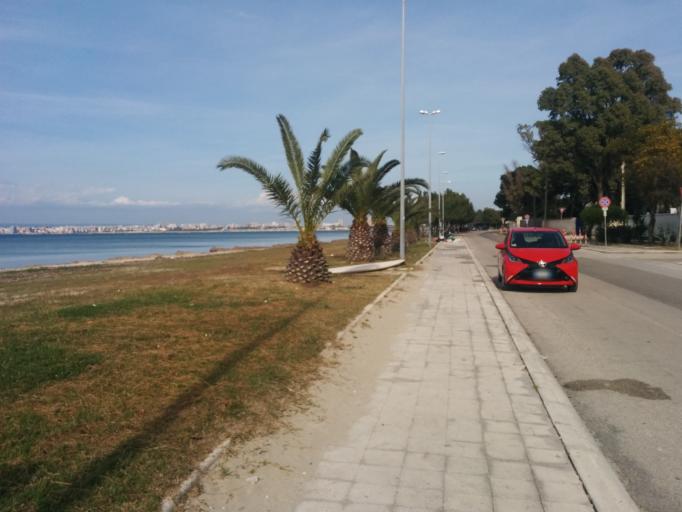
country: IT
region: Apulia
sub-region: Provincia di Taranto
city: Taranto
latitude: 40.4230
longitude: 17.2166
